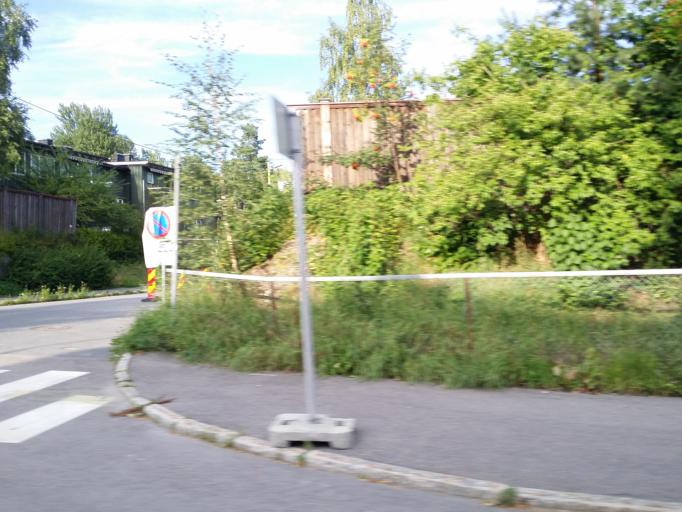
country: NO
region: Akershus
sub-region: Oppegard
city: Kolbotn
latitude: 59.8970
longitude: 10.8532
